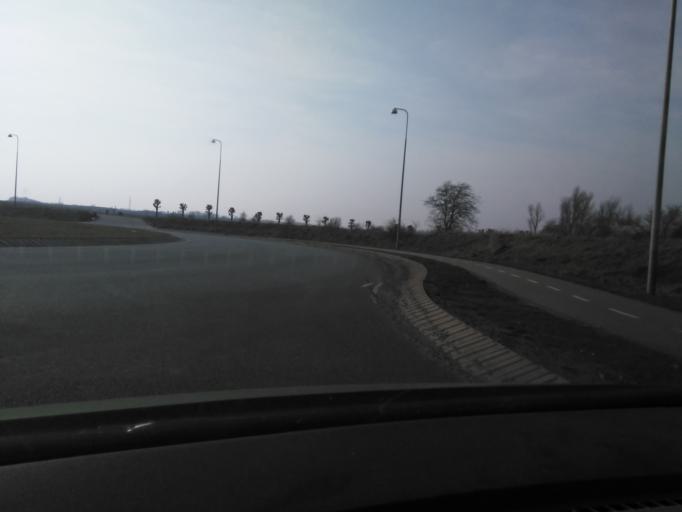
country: DK
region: Central Jutland
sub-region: Arhus Kommune
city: Trige
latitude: 56.2028
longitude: 10.1736
